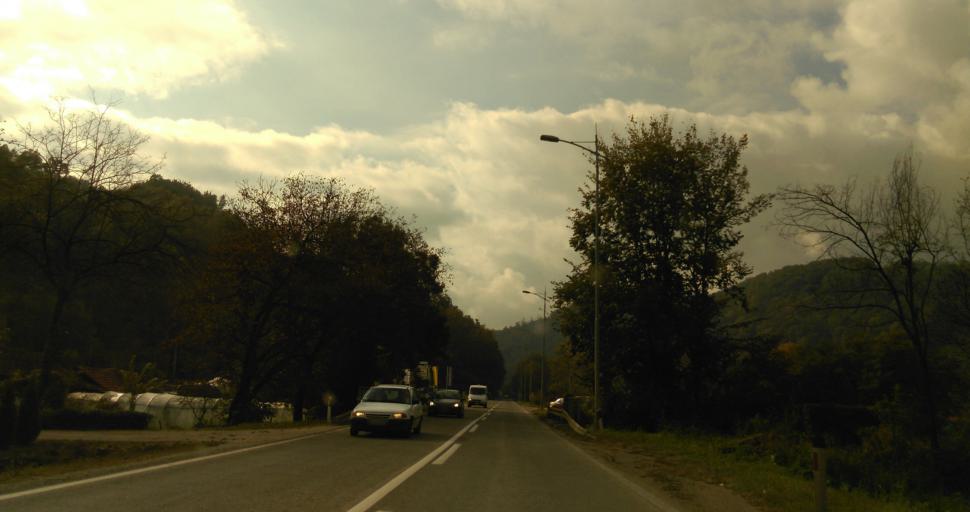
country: RS
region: Central Serbia
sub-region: Kolubarski Okrug
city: Ljig
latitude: 44.2131
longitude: 20.2264
